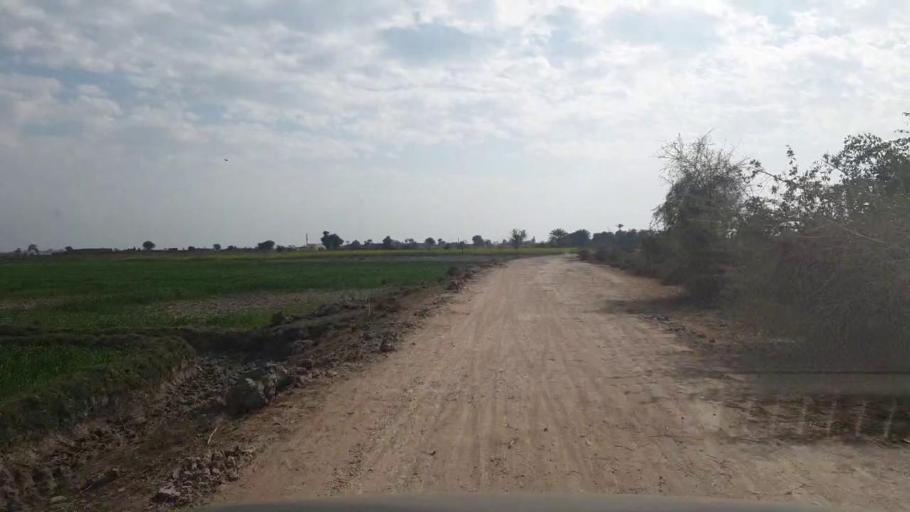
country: PK
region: Sindh
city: Sakrand
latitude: 26.0034
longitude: 68.4048
